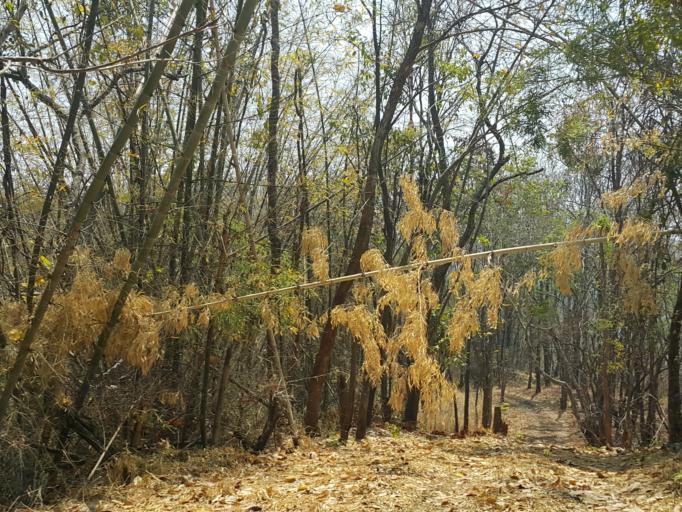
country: TH
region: Chiang Mai
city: Samoeng
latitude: 18.7901
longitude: 98.8235
